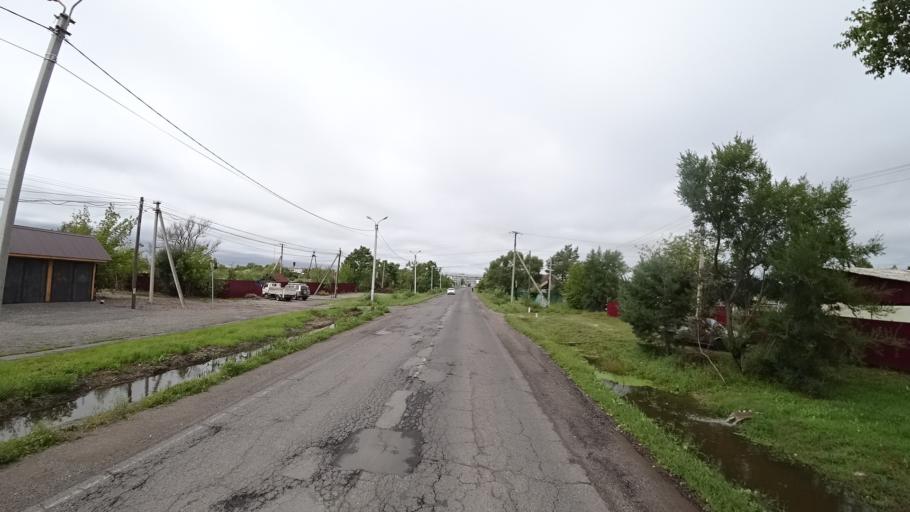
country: RU
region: Primorskiy
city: Monastyrishche
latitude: 44.2018
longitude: 132.4550
